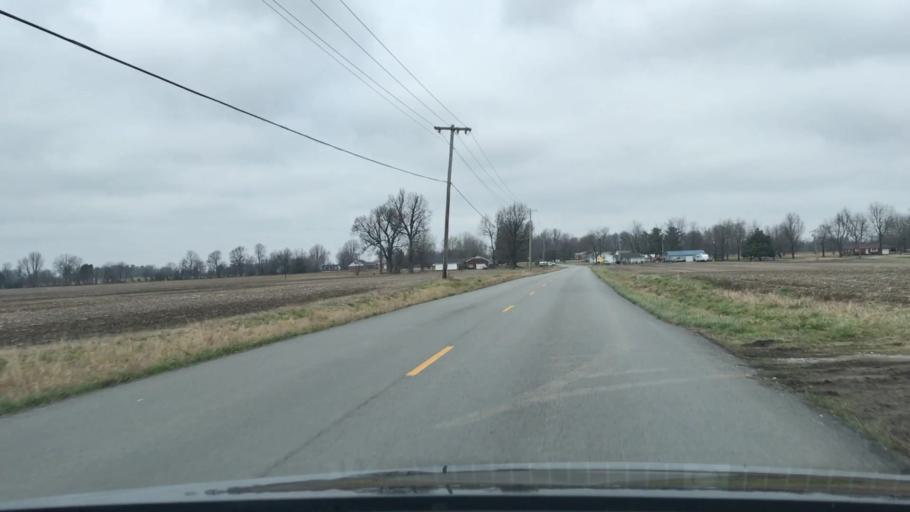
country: US
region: Kentucky
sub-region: Muhlenberg County
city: Morehead
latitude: 37.3538
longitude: -87.2283
